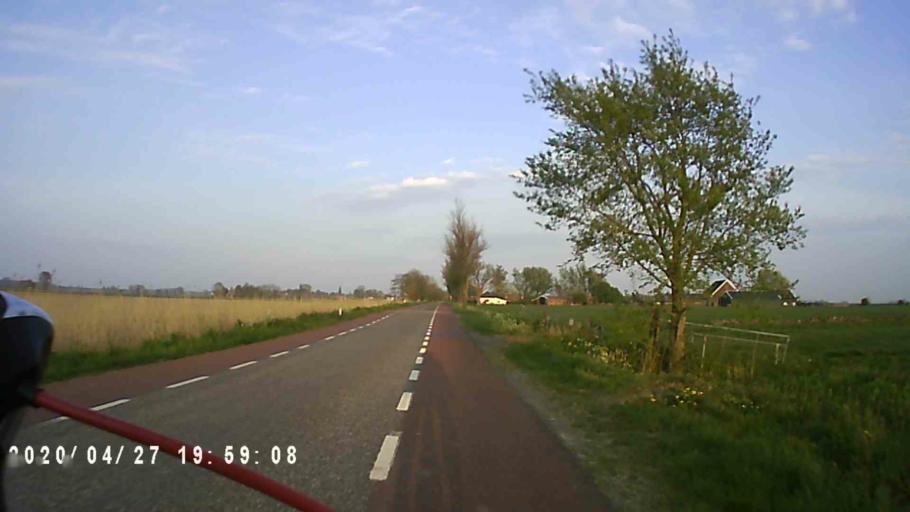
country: NL
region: Groningen
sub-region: Gemeente Zuidhorn
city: Oldehove
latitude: 53.3106
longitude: 6.4284
